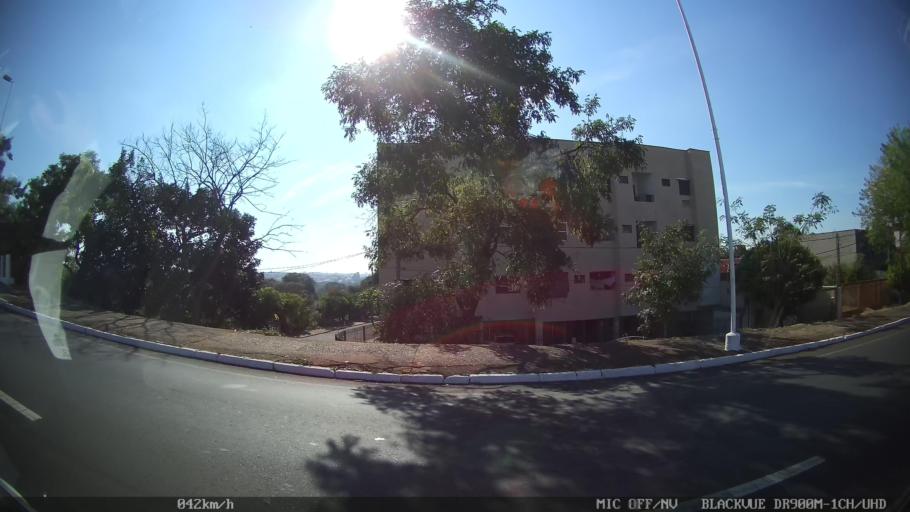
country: BR
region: Sao Paulo
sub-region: Sao Jose Do Rio Preto
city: Sao Jose do Rio Preto
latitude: -20.8042
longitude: -49.4046
